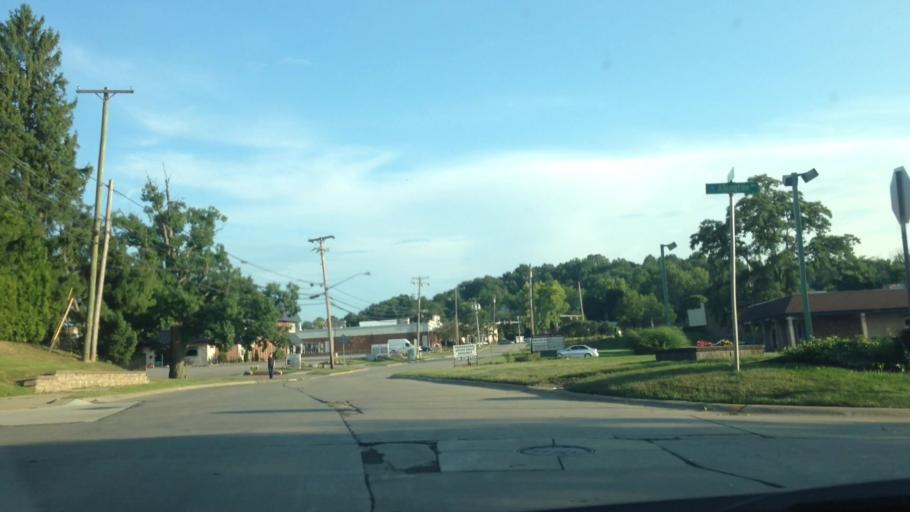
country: US
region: Ohio
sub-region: Summit County
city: Fairlawn
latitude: 41.1291
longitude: -81.6070
